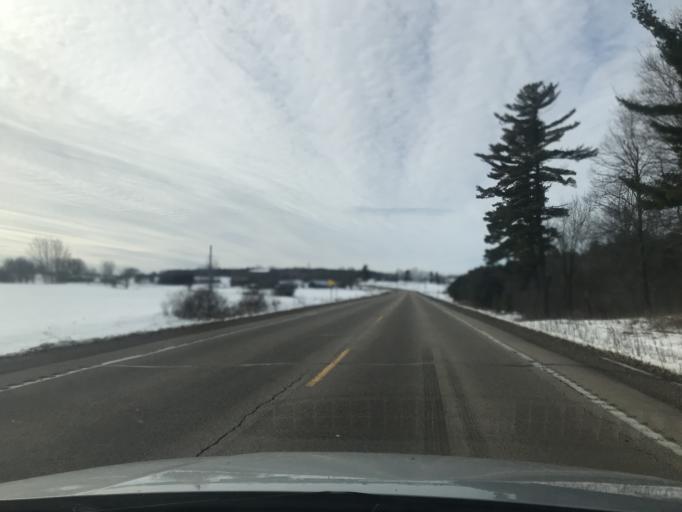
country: US
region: Wisconsin
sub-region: Oconto County
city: Gillett
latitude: 44.8820
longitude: -88.3421
